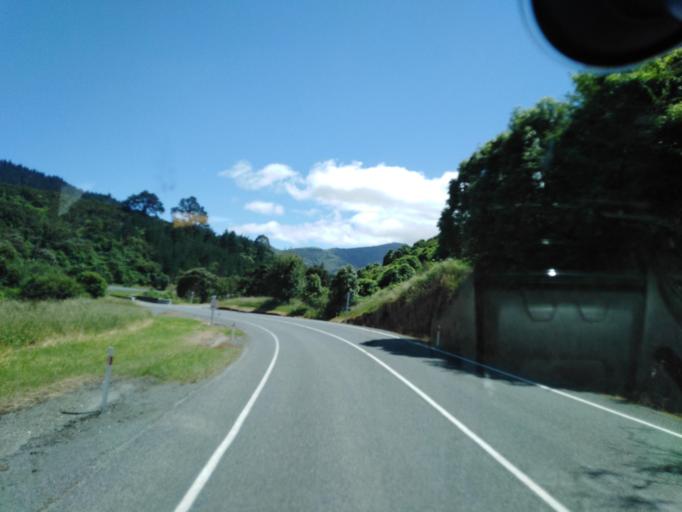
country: NZ
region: Nelson
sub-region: Nelson City
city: Nelson
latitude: -41.2272
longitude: 173.3974
